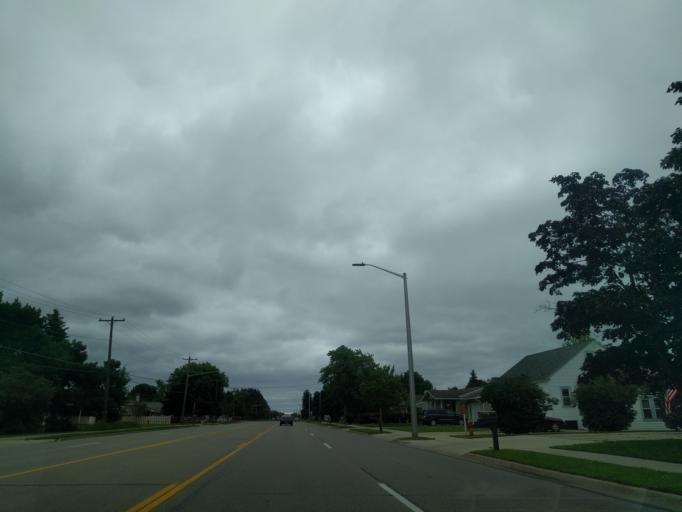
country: US
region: Michigan
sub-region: Delta County
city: Escanaba
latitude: 45.7334
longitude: -87.0799
